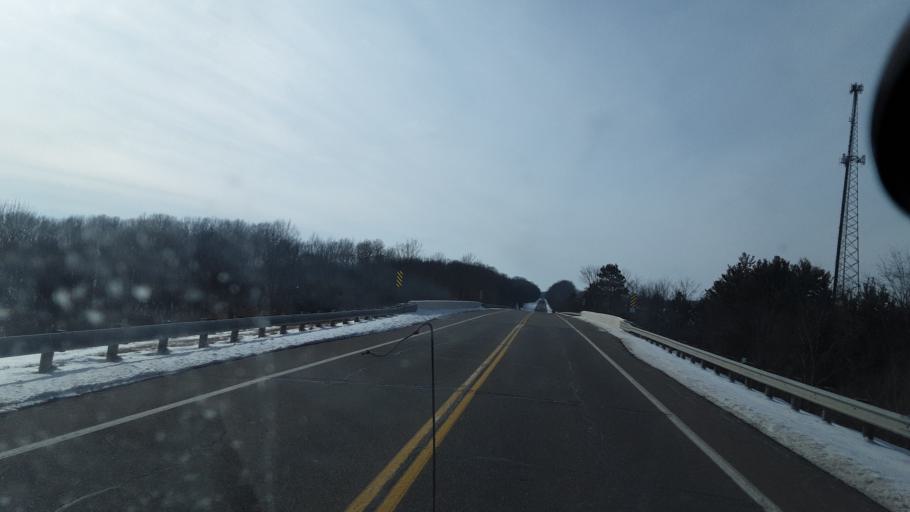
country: US
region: Ohio
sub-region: Stark County
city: Alliance
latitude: 41.0332
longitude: -81.1672
